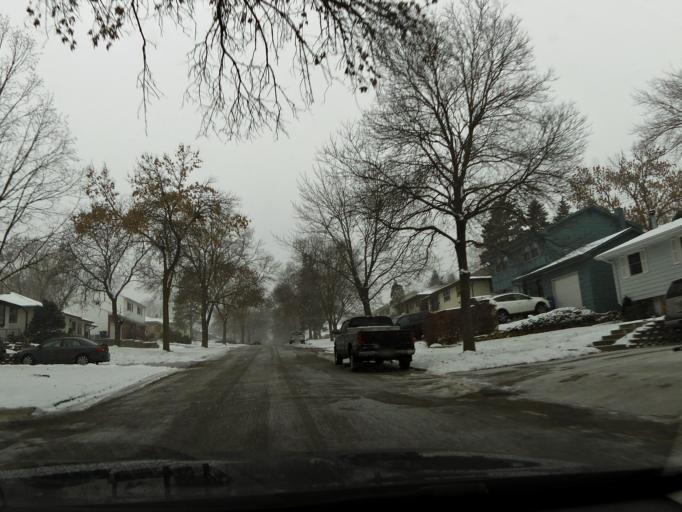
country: US
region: Minnesota
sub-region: Ramsey County
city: Maplewood
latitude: 44.9476
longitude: -93.0266
